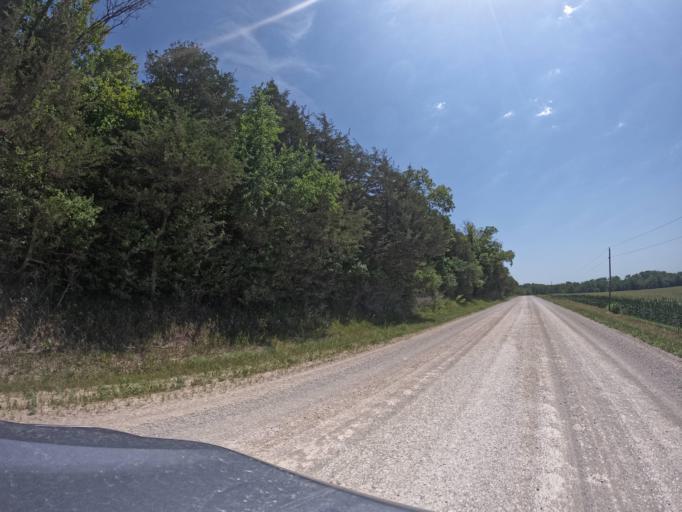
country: US
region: Iowa
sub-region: Henry County
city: Mount Pleasant
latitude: 40.8901
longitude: -91.5416
